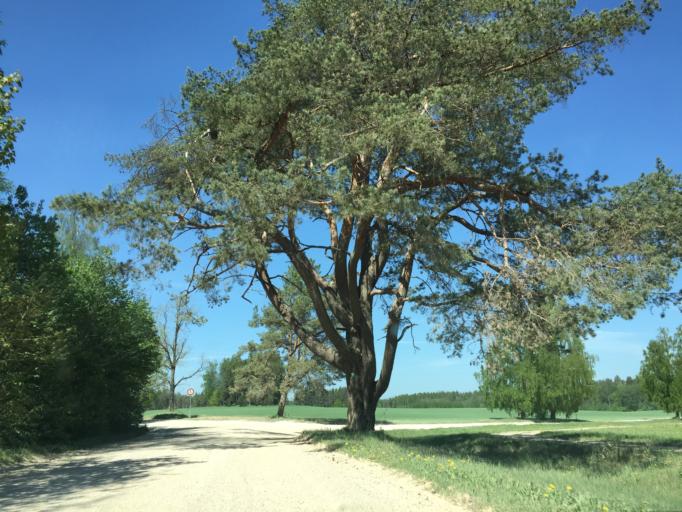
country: LV
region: Ikskile
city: Ikskile
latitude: 56.8588
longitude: 24.5010
